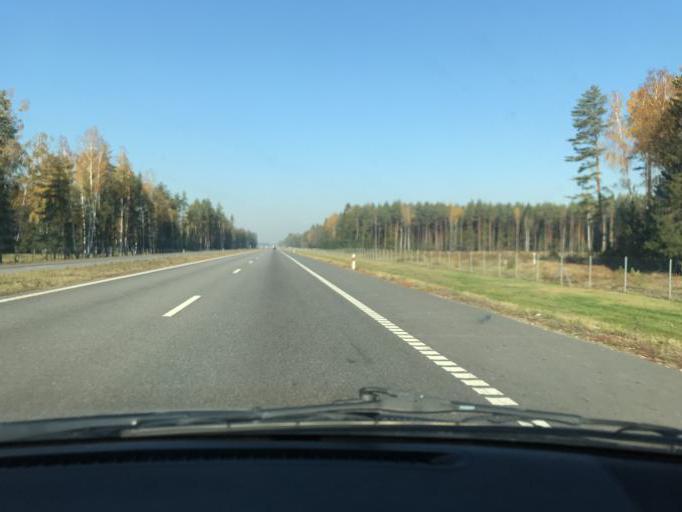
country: BY
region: Minsk
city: Slutsk
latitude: 53.3041
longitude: 27.5421
